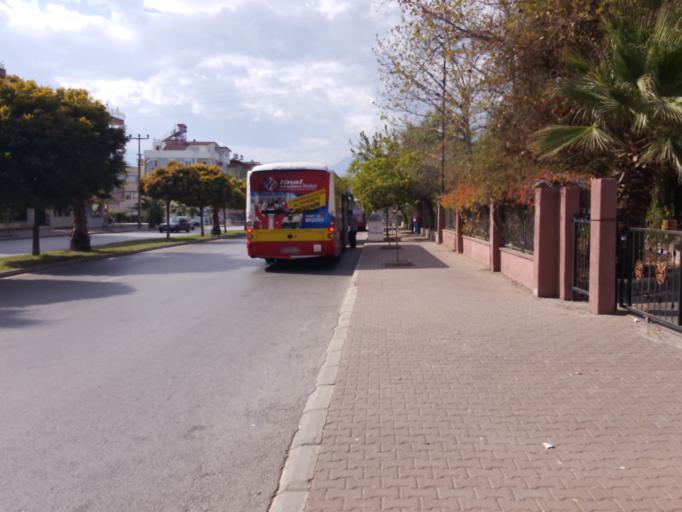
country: TR
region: Antalya
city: Antalya
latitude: 36.9101
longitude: 30.6465
